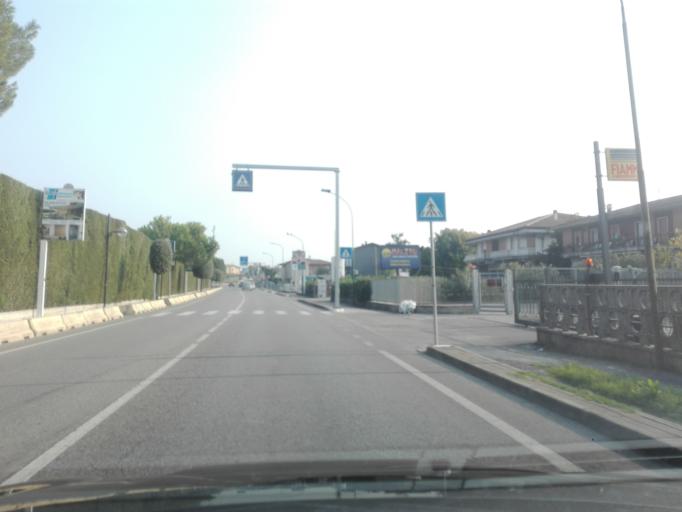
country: IT
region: Veneto
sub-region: Provincia di Verona
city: Peschiera del Garda
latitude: 45.4437
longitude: 10.6731
